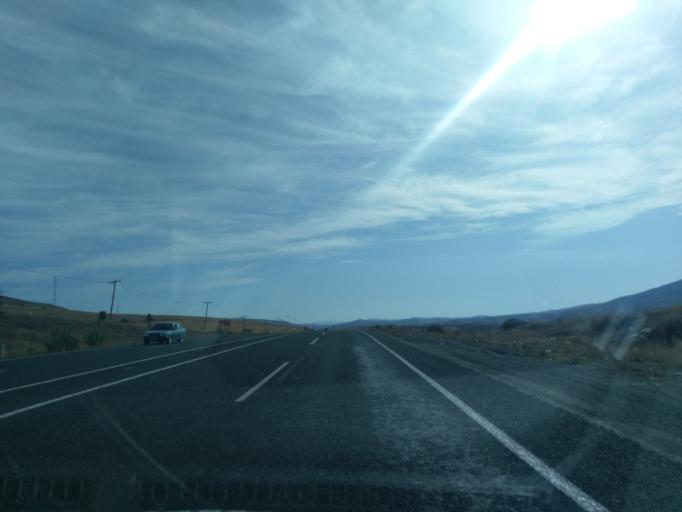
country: TR
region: Sivas
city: Zara
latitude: 39.8611
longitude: 37.8802
